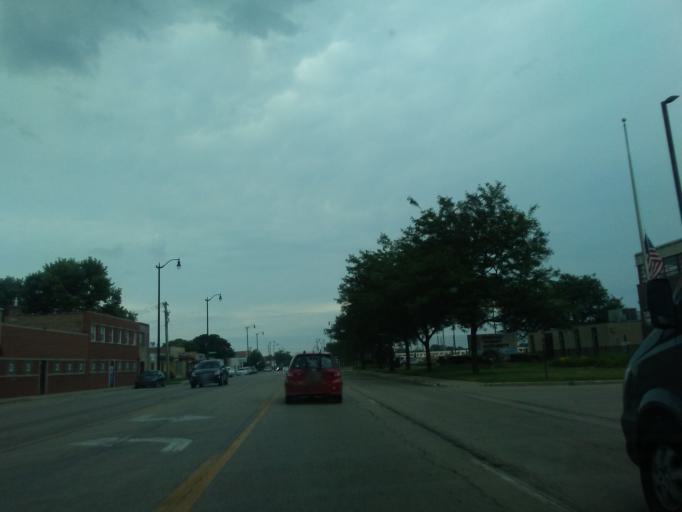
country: US
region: Illinois
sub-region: Cook County
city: Skokie
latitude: 42.0263
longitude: -87.7230
